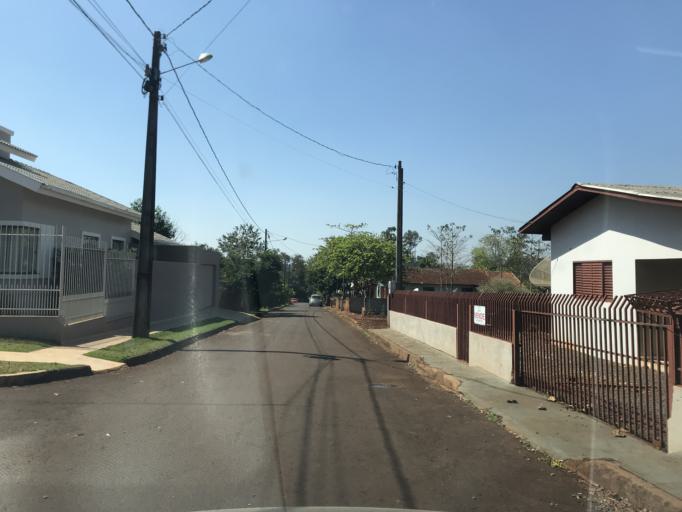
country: BR
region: Parana
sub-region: Palotina
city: Palotina
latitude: -24.3009
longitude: -53.8319
